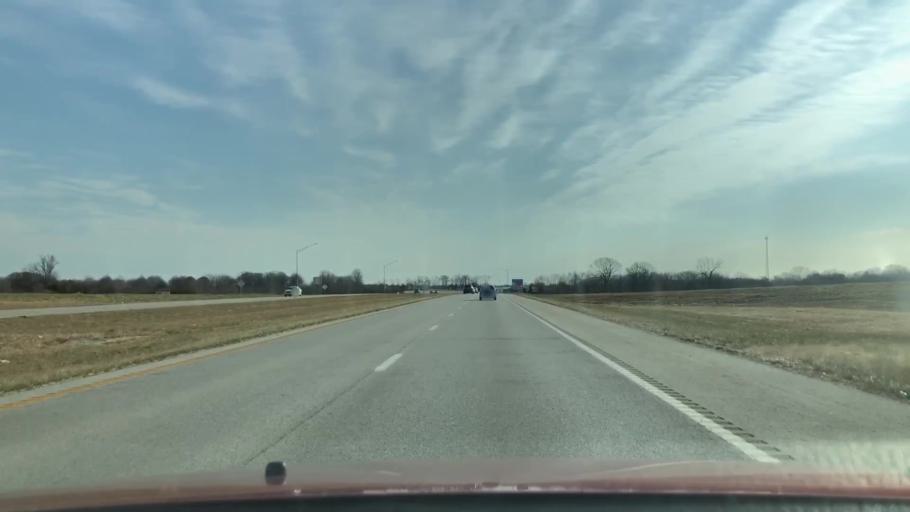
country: US
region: Missouri
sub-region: Webster County
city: Rogersville
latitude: 37.1126
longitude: -93.0728
